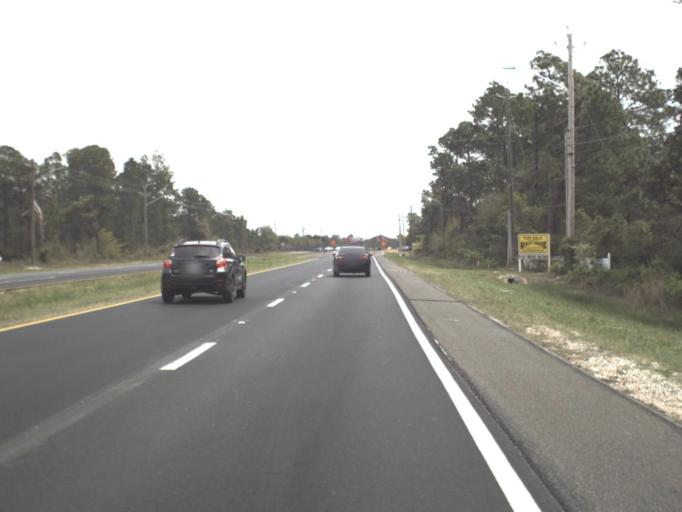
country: US
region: Florida
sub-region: Santa Rosa County
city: Woodlawn Beach
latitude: 30.4037
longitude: -86.9623
